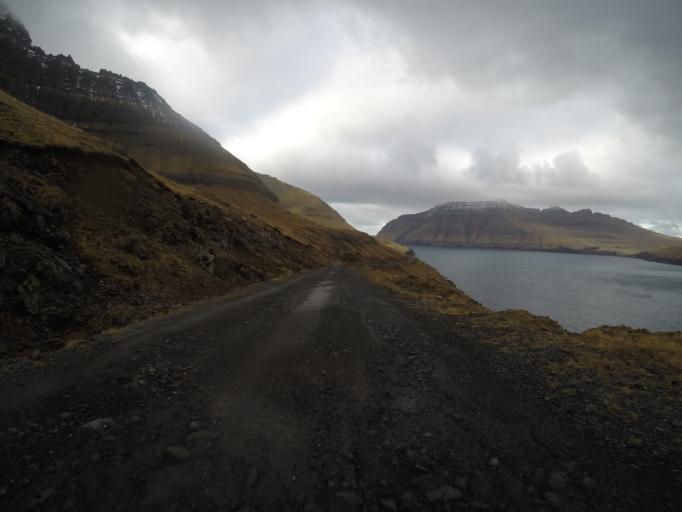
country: FO
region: Nordoyar
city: Klaksvik
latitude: 62.3392
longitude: -6.5803
